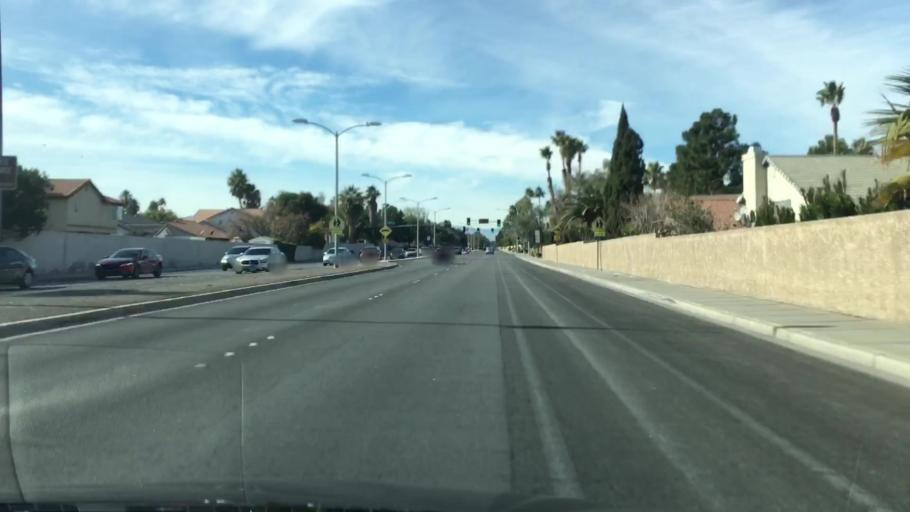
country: US
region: Nevada
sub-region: Clark County
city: Whitney
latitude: 36.0563
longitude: -115.0665
